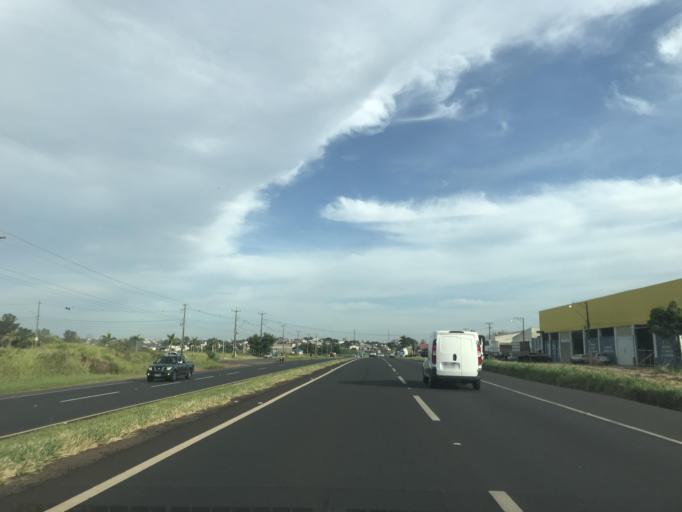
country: BR
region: Parana
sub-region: Mandaguacu
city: Mandaguacu
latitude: -23.3621
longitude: -52.0857
